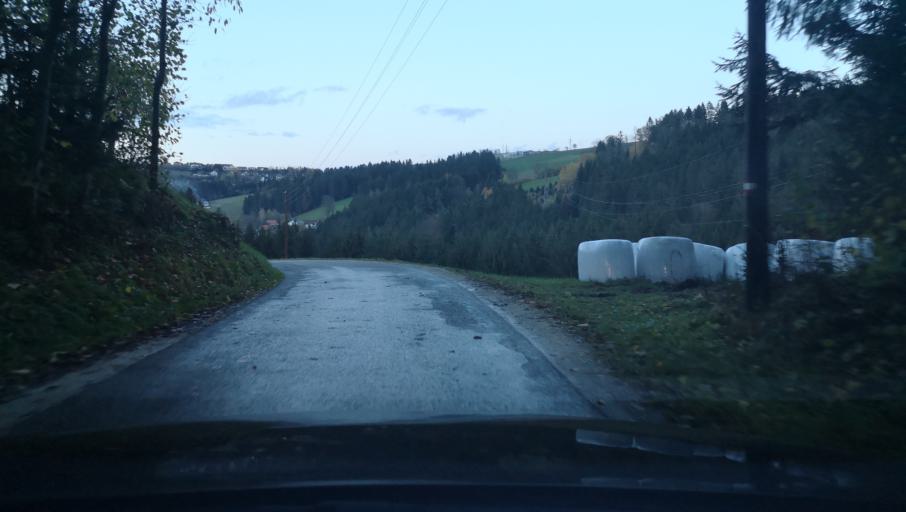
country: AT
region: Styria
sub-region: Politischer Bezirk Weiz
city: Birkfeld
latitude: 47.3361
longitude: 15.6842
